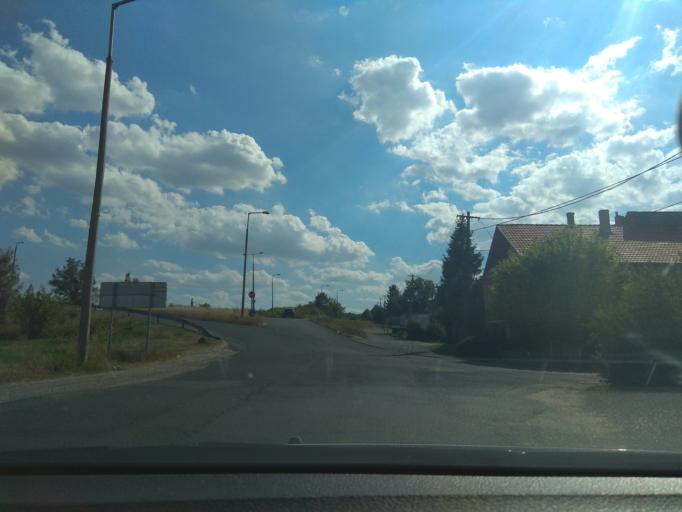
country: HU
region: Borsod-Abauj-Zemplen
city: Miskolc
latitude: 48.0526
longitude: 20.7975
